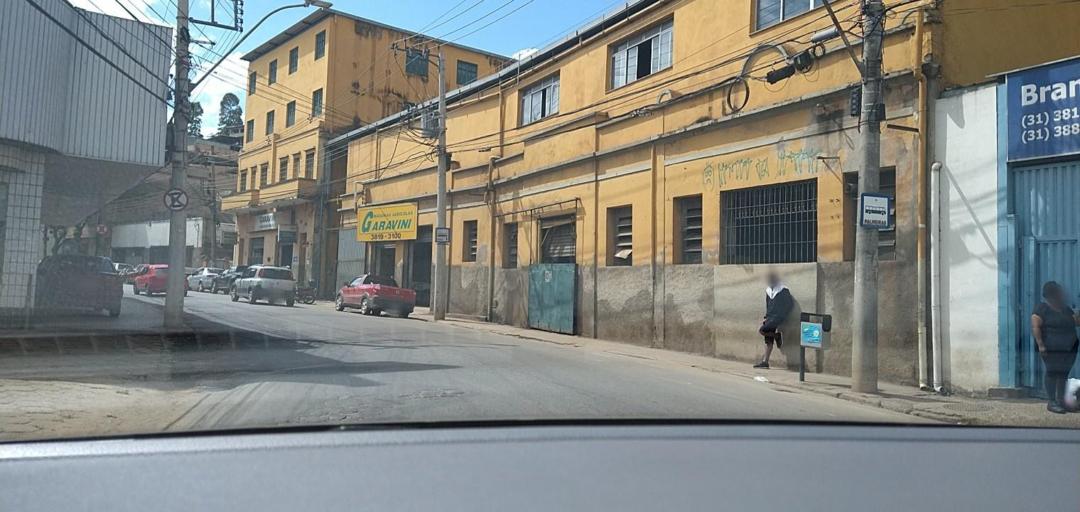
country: BR
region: Minas Gerais
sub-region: Ponte Nova
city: Ponte Nova
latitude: -20.4151
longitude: -42.8998
